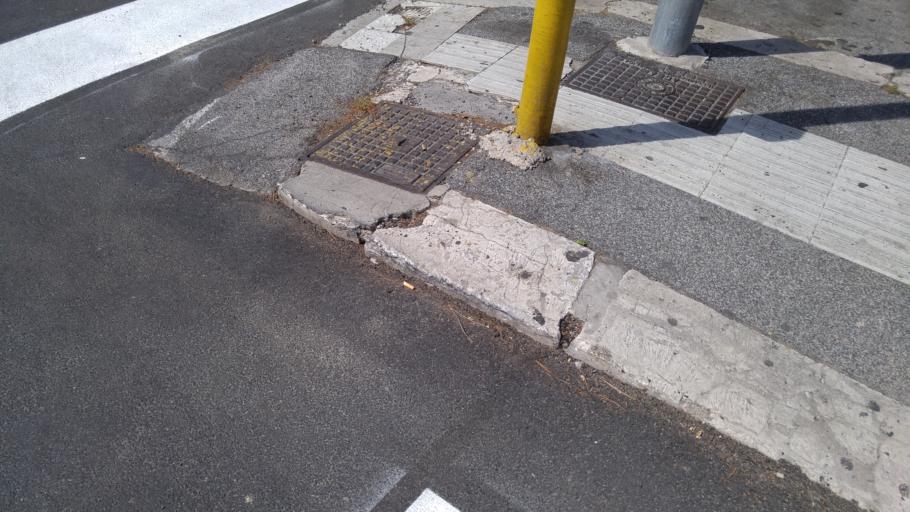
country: IT
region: Latium
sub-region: Citta metropolitana di Roma Capitale
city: Rome
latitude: 41.8691
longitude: 12.5301
